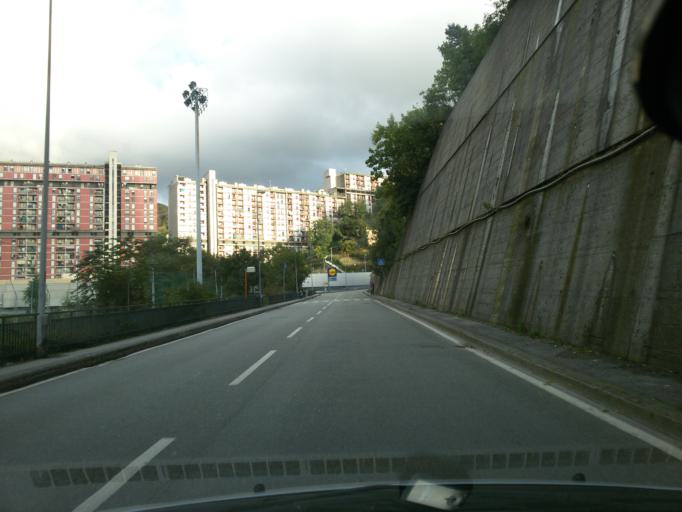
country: IT
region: Liguria
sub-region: Provincia di Genova
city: Genoa
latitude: 44.4523
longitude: 8.9023
